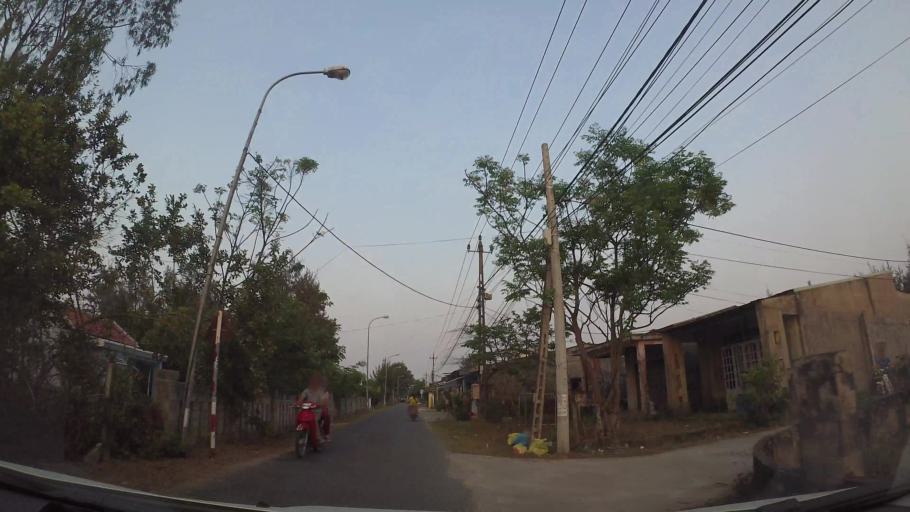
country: VN
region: Da Nang
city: Ngu Hanh Son
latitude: 15.9724
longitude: 108.2404
